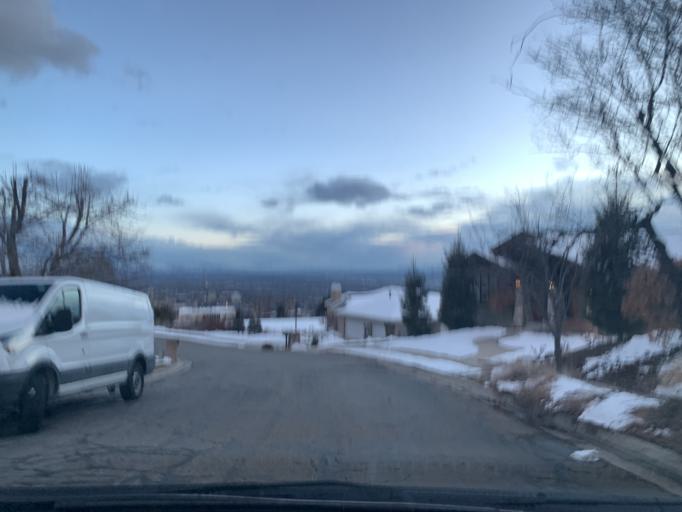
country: US
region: Utah
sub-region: Salt Lake County
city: Salt Lake City
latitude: 40.7831
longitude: -111.8525
